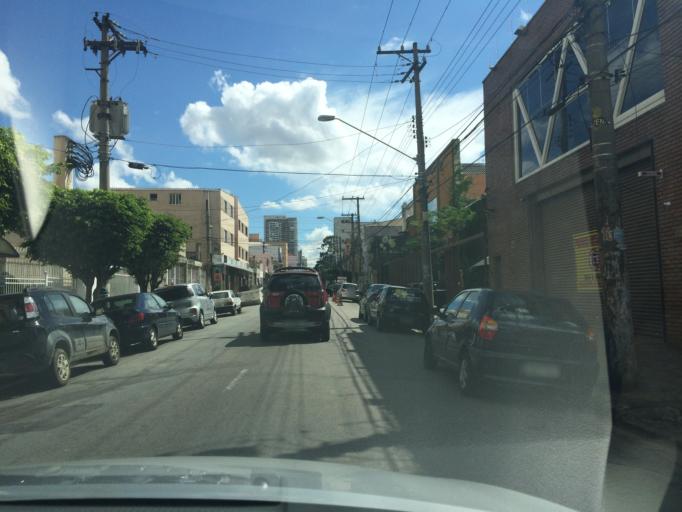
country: BR
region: Sao Paulo
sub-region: Guarulhos
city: Guarulhos
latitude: -23.5409
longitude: -46.5528
